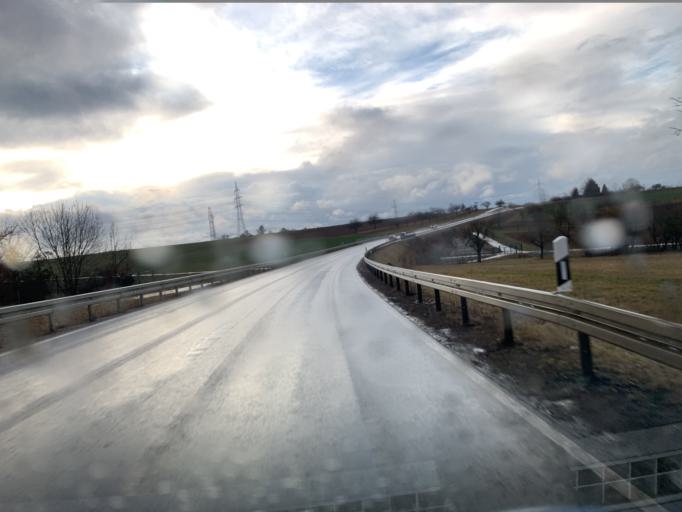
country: DE
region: Baden-Wuerttemberg
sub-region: Regierungsbezirk Stuttgart
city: Magstadt
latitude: 48.7339
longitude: 8.9617
